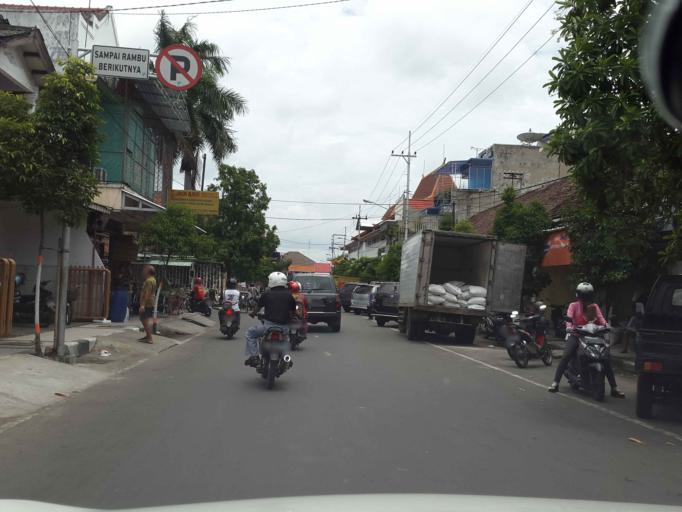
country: ID
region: East Java
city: Mojokerto
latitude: -7.4682
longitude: 112.4350
